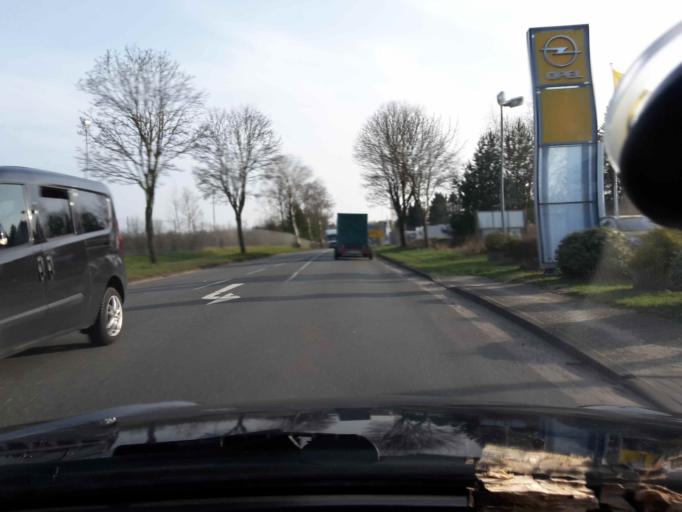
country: DE
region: Lower Saxony
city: Hollenstedt
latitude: 53.3623
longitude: 9.7111
